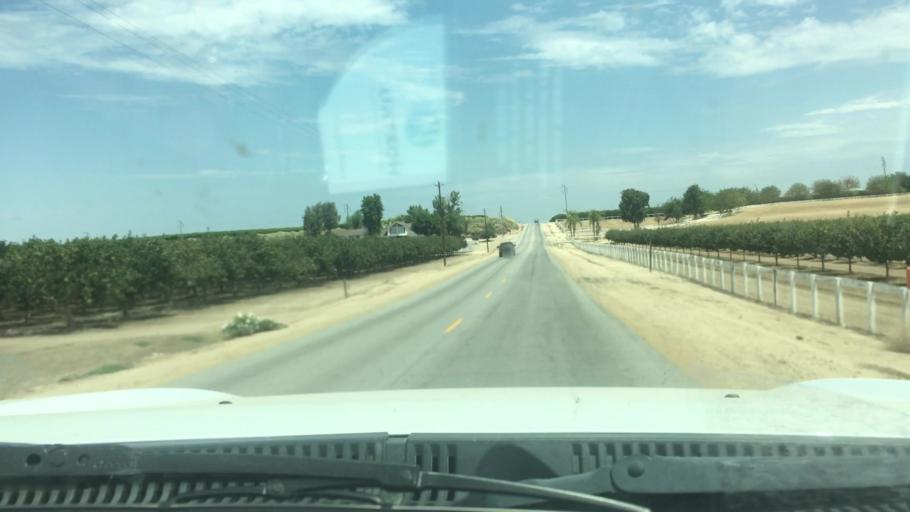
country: US
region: California
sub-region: Kern County
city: Shafter
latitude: 35.5632
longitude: -119.1511
